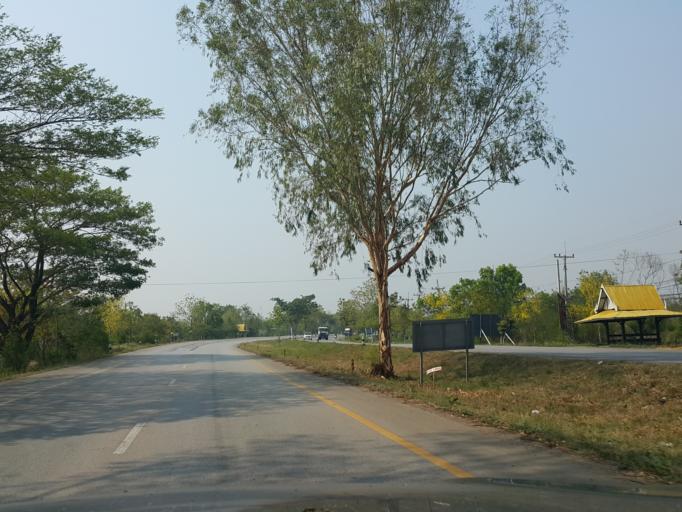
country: TH
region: Lampang
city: Ko Kha
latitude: 18.1827
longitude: 99.4088
